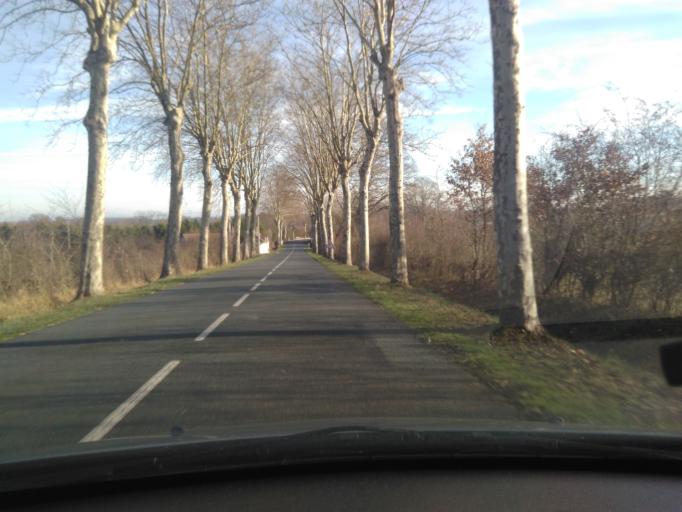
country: FR
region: Centre
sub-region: Departement du Cher
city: Le Chatelet
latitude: 46.6441
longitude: 2.2702
